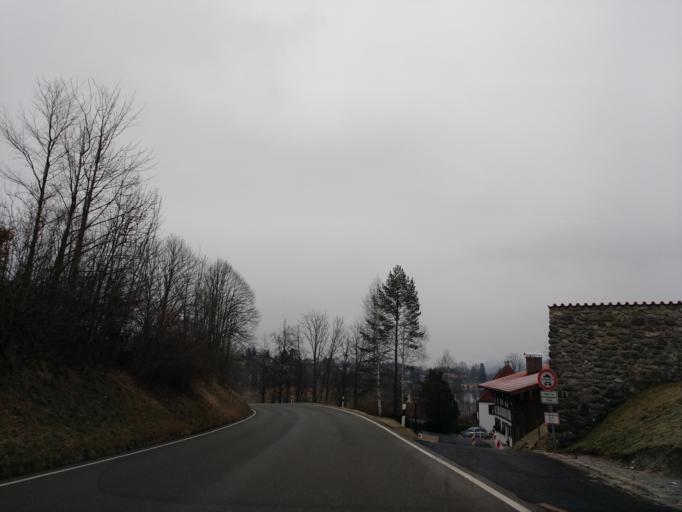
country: AT
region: Tyrol
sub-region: Politischer Bezirk Reutte
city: Vils
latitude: 47.5734
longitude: 10.6399
